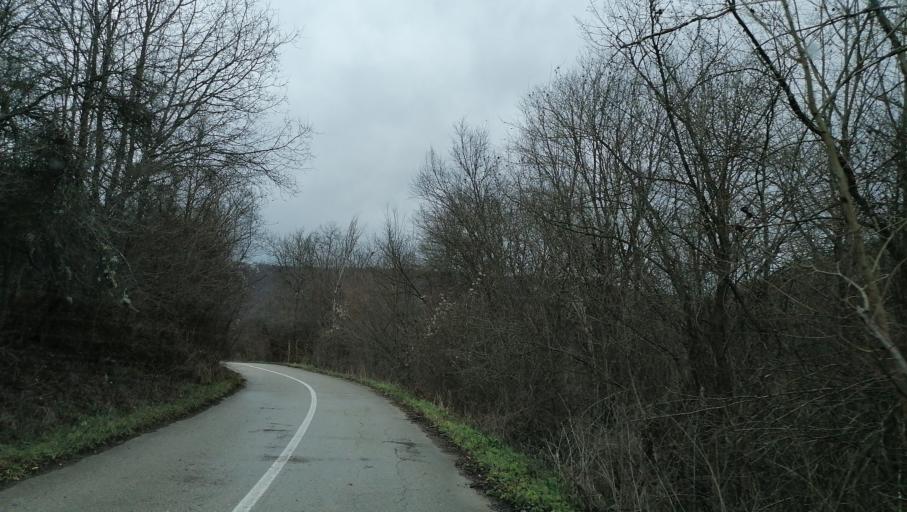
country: RS
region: Central Serbia
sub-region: Pirotski Okrug
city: Dimitrovgrad
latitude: 42.9283
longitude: 22.7708
